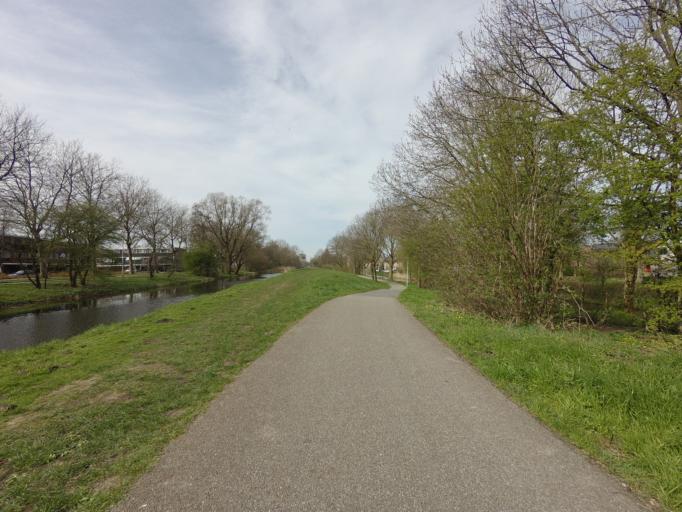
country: NL
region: South Holland
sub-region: Gemeente Alphen aan den Rijn
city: Alphen aan den Rijn
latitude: 52.1481
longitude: 4.6691
